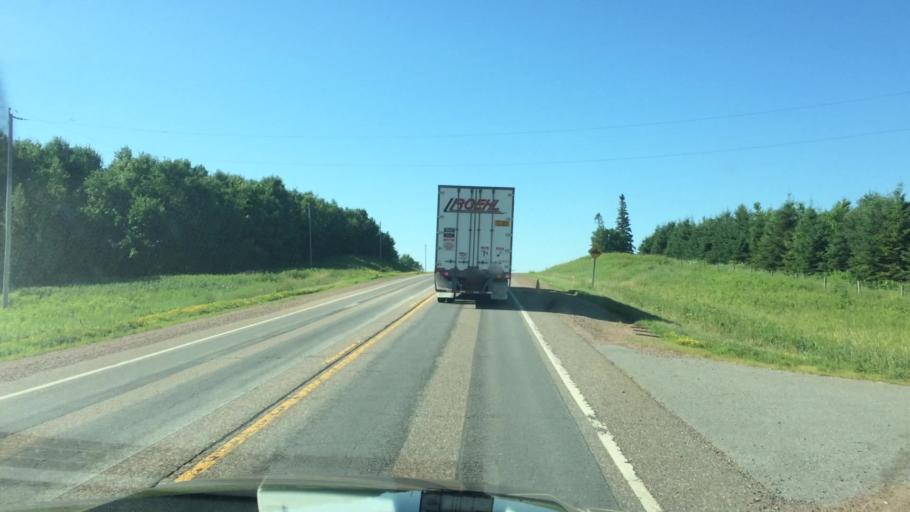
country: US
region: Wisconsin
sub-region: Marathon County
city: Athens
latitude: 44.9269
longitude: -90.0788
